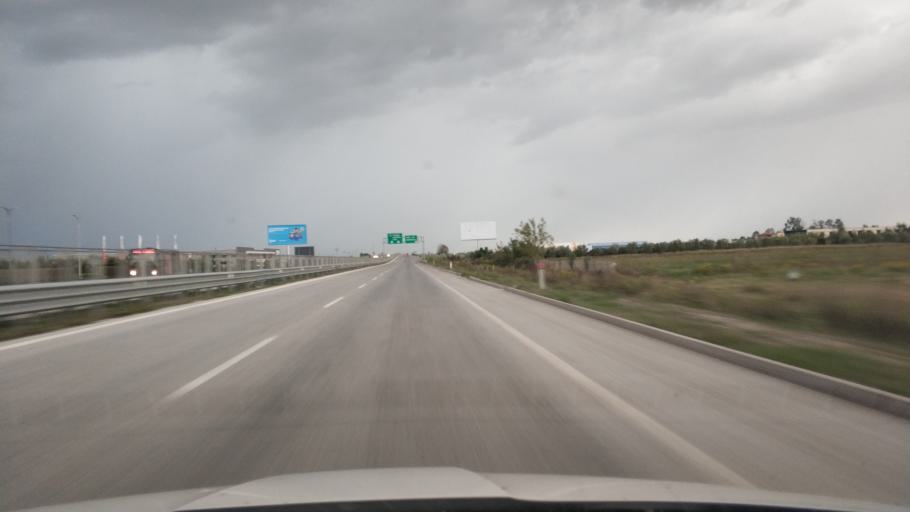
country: AL
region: Vlore
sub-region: Rrethi i Vlores
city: Novosele
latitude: 40.6100
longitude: 19.4740
